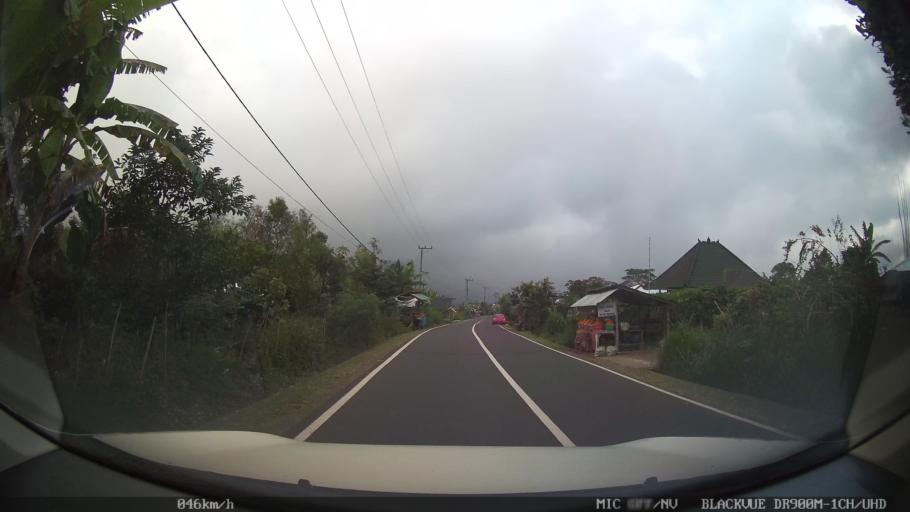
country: ID
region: Bali
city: Banjar Kedisan
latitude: -8.2736
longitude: 115.3298
